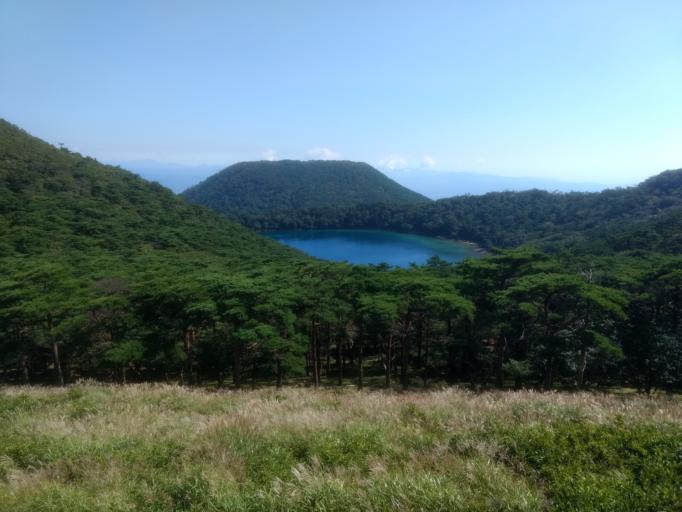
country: JP
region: Miyazaki
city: Kobayashi
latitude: 31.9529
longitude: 130.8415
